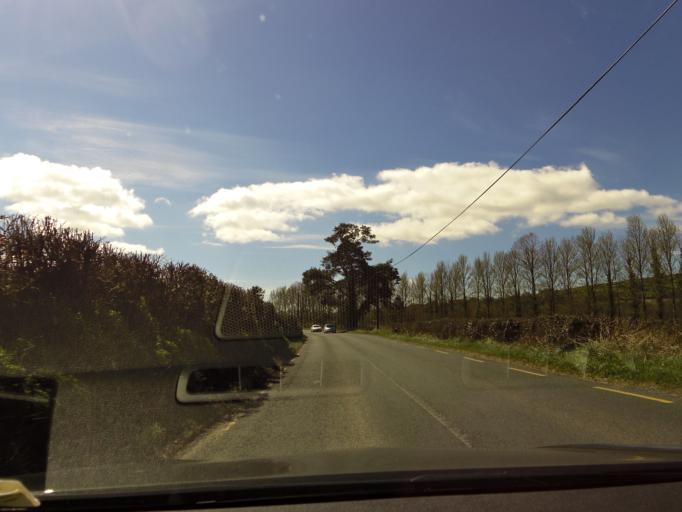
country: IE
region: Leinster
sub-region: Wicklow
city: Aughrim
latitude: 52.8065
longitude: -6.4246
